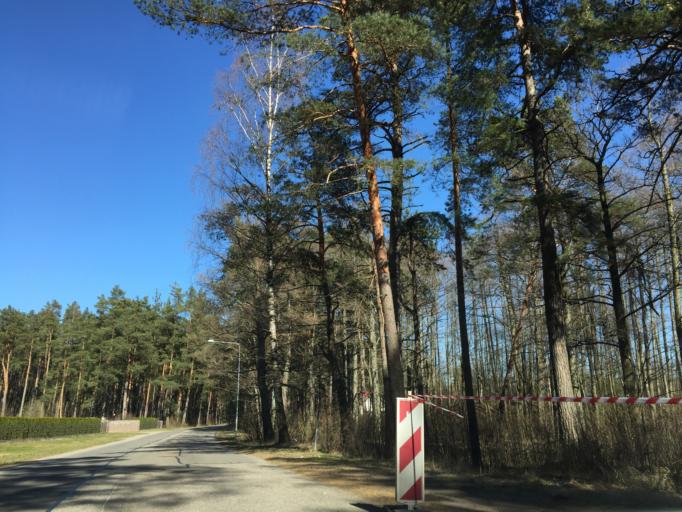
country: LV
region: Babite
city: Pinki
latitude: 56.9879
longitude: 23.9046
